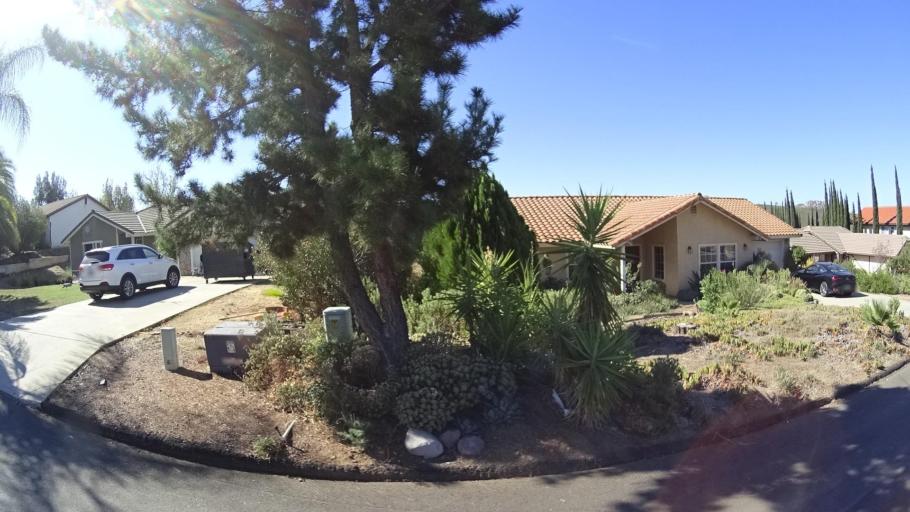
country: US
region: California
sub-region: San Diego County
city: San Diego Country Estates
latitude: 33.0026
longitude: -116.7692
